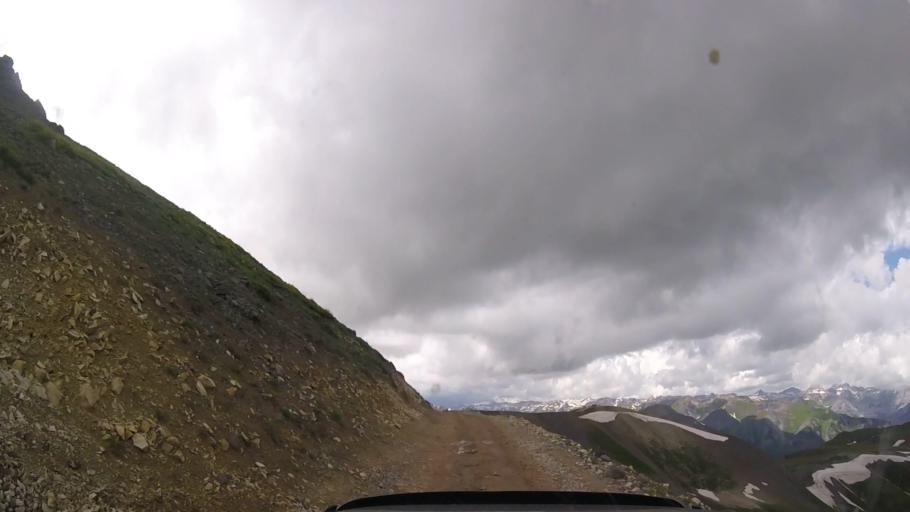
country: US
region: Colorado
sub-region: Ouray County
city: Ouray
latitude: 37.9711
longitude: -107.5891
